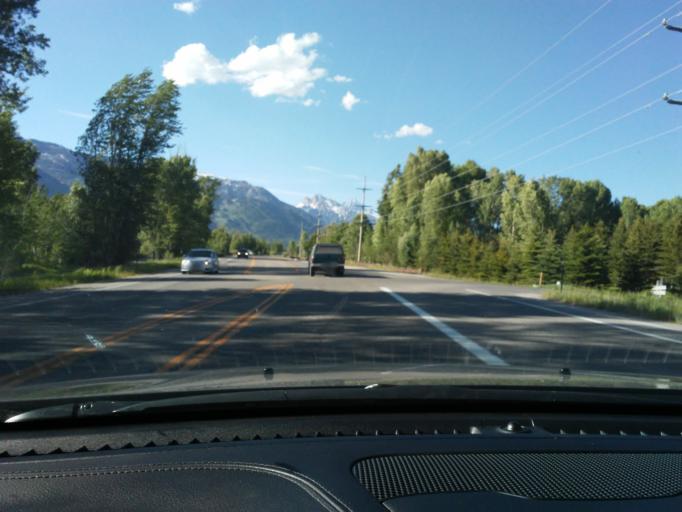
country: US
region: Wyoming
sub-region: Teton County
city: Moose Wilson Road
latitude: 43.5454
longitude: -110.8220
